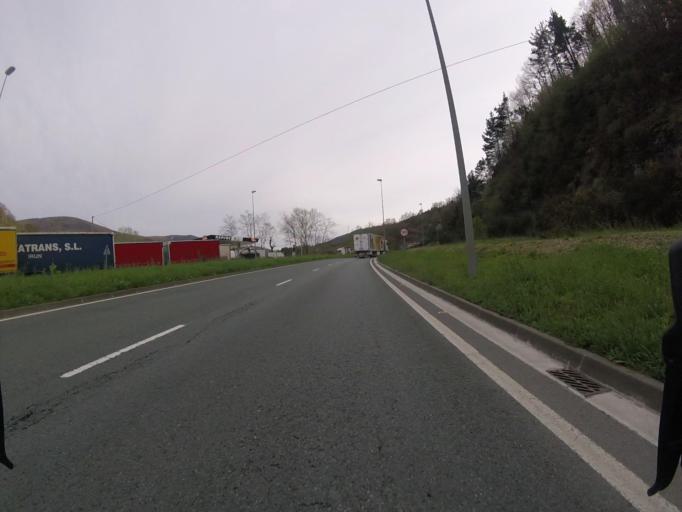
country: ES
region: Basque Country
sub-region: Provincia de Guipuzcoa
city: Irun
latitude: 43.3364
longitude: -1.7534
